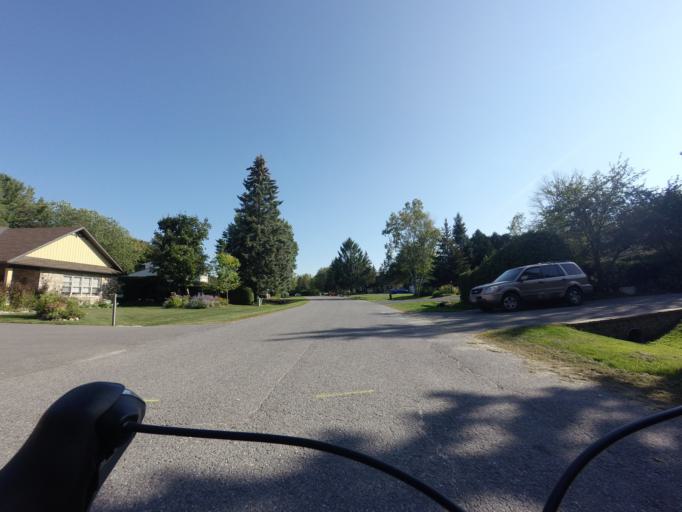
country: CA
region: Ontario
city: Bells Corners
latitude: 45.2333
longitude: -75.6852
